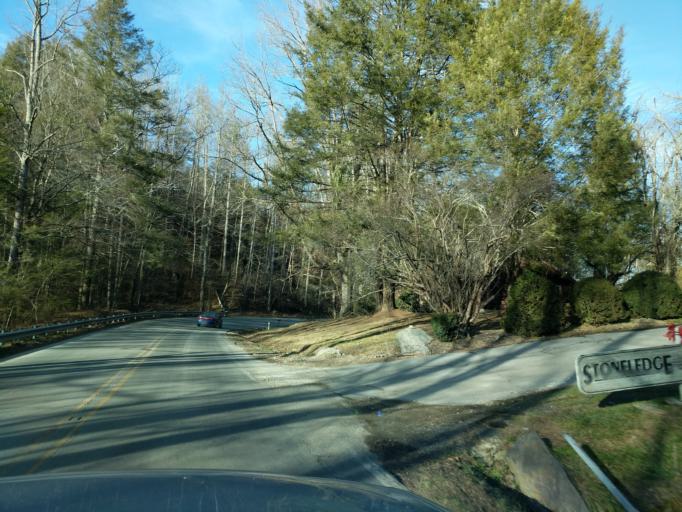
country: US
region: North Carolina
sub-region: Henderson County
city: Edneyville
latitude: 35.4168
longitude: -82.3126
